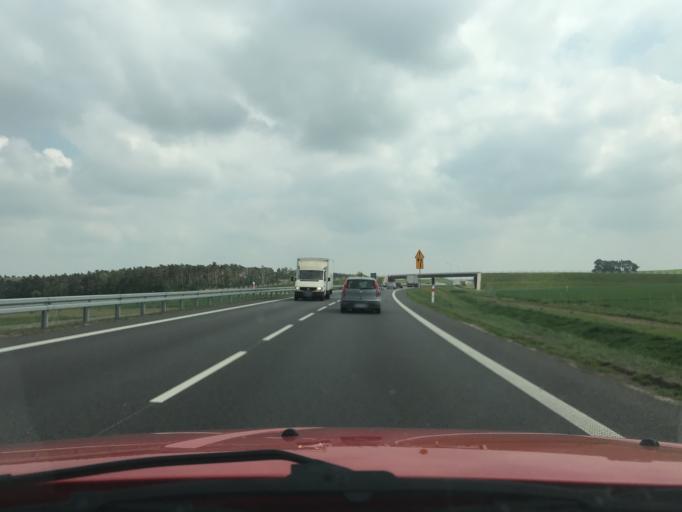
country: PL
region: Greater Poland Voivodeship
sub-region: Powiat sredzki
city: Nowe Miasto nad Warta
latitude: 52.0427
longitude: 17.4594
